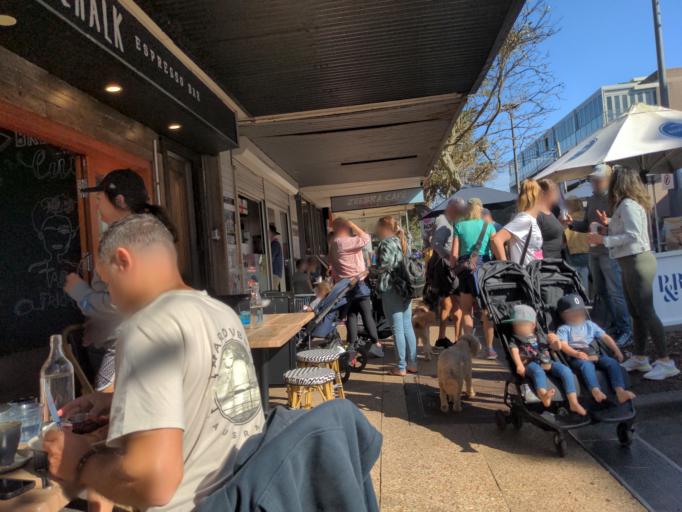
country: AU
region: New South Wales
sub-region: Randwick
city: South Coogee
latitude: -33.9462
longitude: 151.2562
